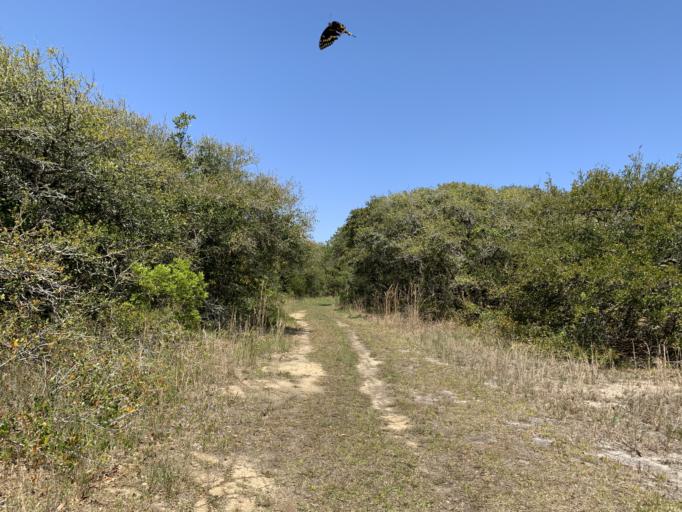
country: US
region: North Carolina
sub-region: Dare County
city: Southern Shores
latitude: 36.2372
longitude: -75.7787
